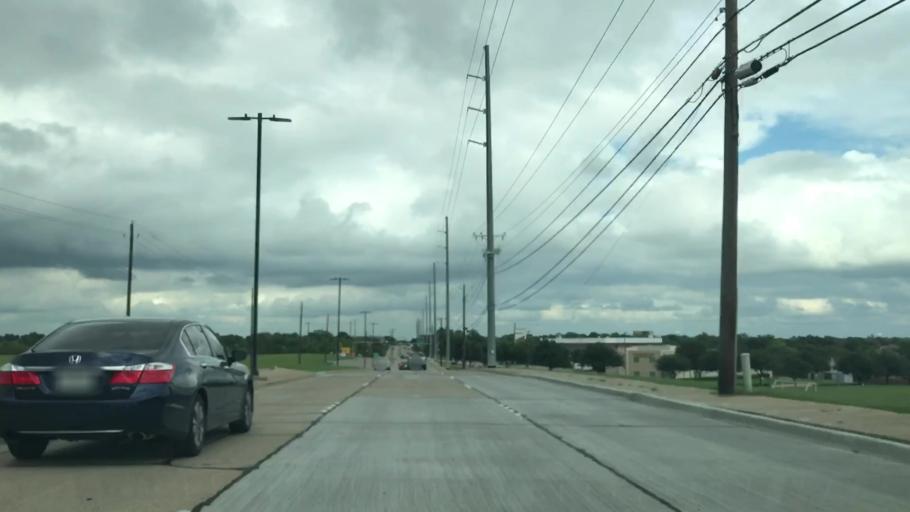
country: US
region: Texas
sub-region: Dallas County
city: Garland
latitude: 32.8846
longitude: -96.6142
